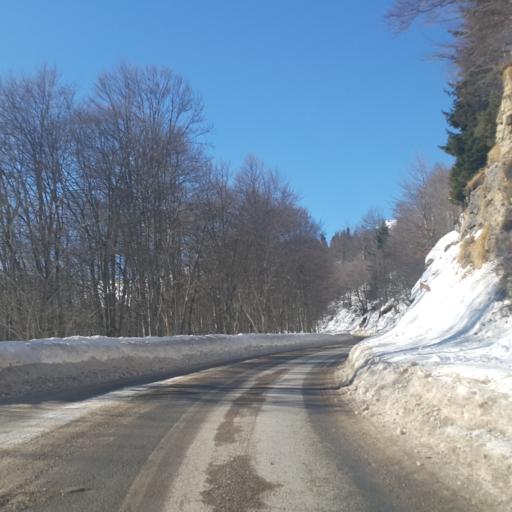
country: XK
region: Mitrovica
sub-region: Komuna e Leposaviqit
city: Leposaviq
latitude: 43.3147
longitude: 20.8552
